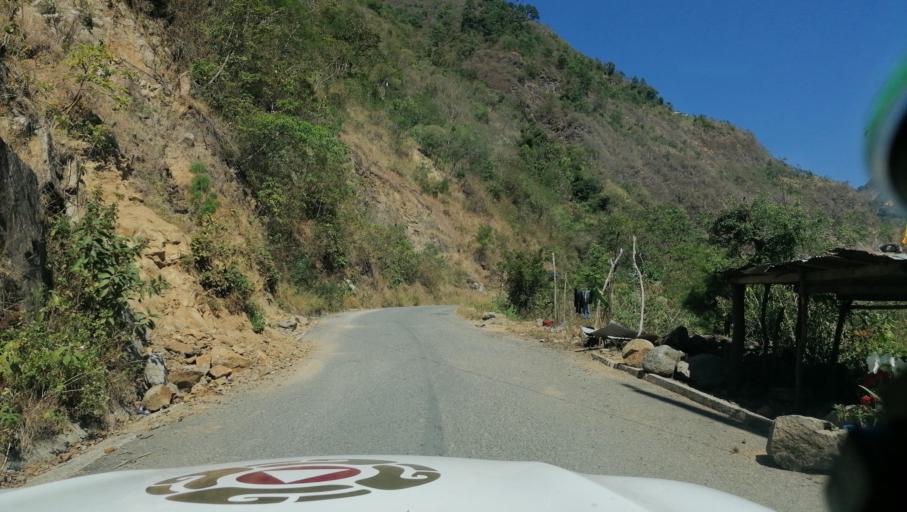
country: GT
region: San Marcos
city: Tacana
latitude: 15.1856
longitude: -92.1851
